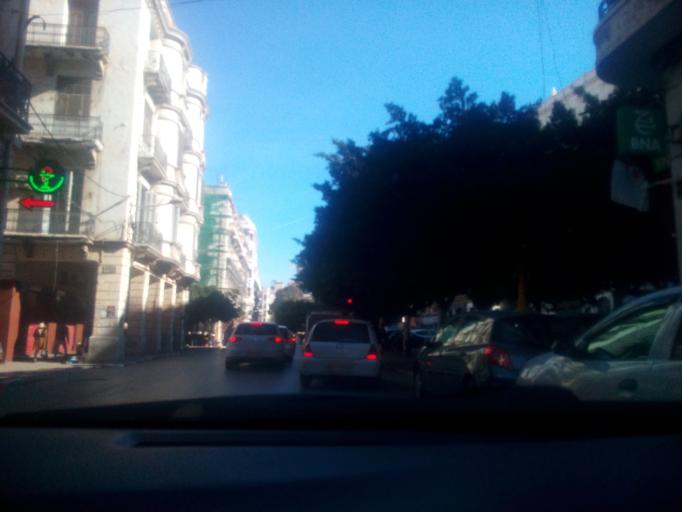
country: DZ
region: Oran
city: Oran
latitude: 35.7029
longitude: -0.6382
